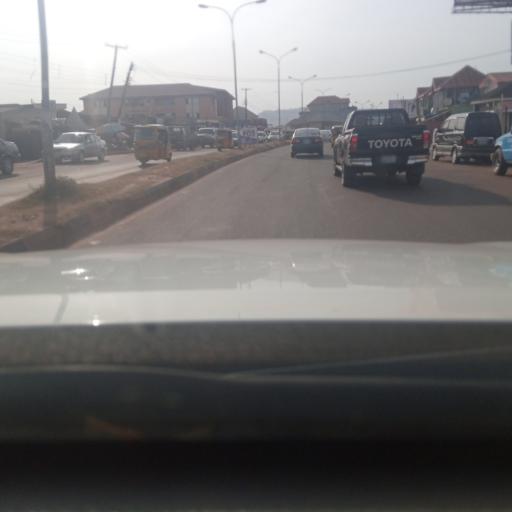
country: NG
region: Enugu
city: Enugu
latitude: 6.4404
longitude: 7.5053
